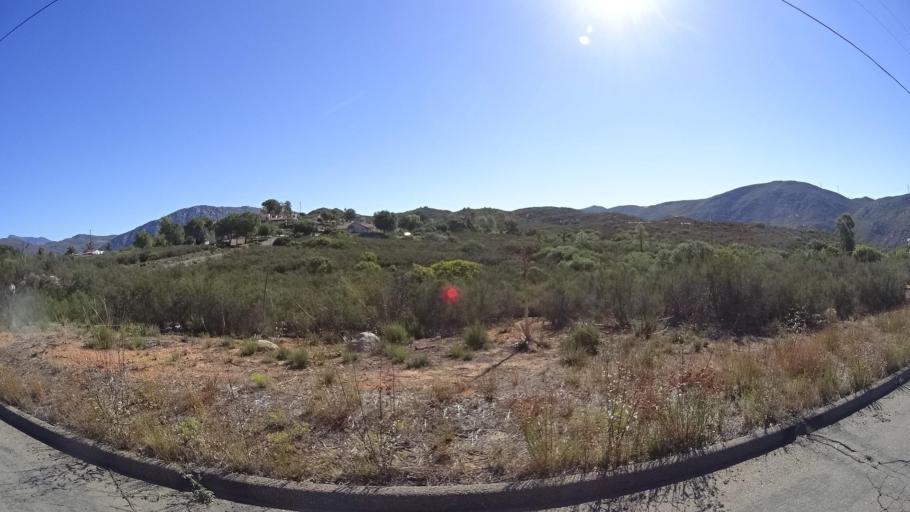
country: US
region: California
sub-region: San Diego County
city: Alpine
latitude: 32.8319
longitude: -116.7008
